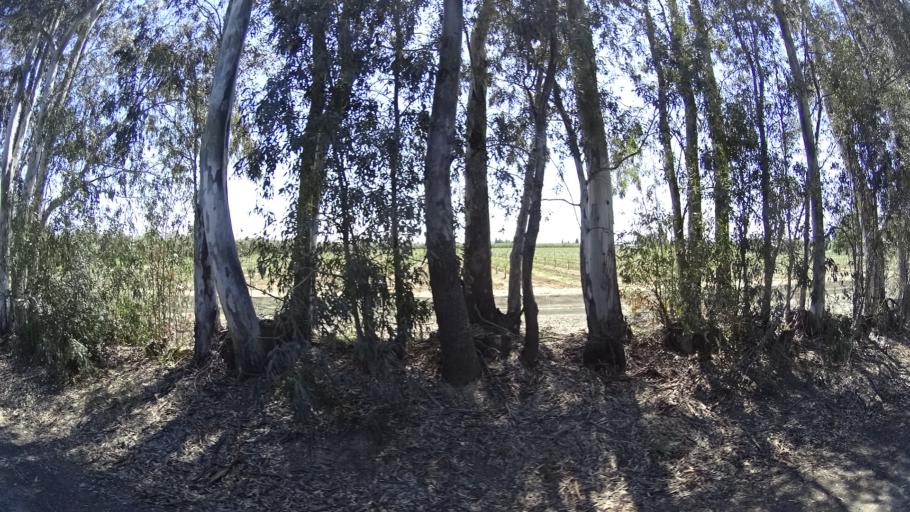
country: US
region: California
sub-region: Glenn County
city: Orland
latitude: 39.7330
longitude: -122.1999
